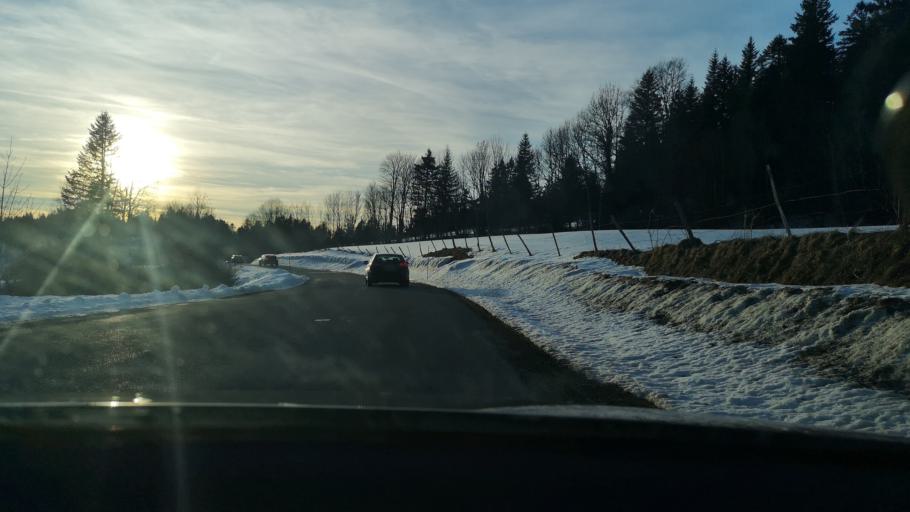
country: FR
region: Franche-Comte
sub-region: Departement du Doubs
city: Gilley
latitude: 46.9887
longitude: 6.5136
